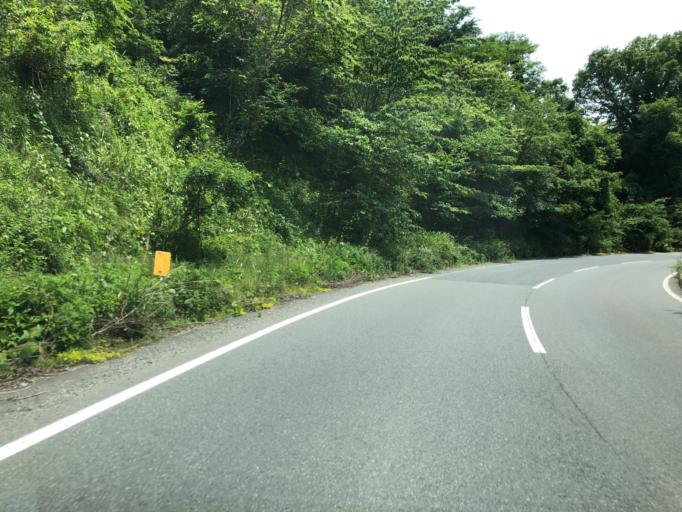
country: JP
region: Fukushima
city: Namie
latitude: 37.5893
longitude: 140.9368
